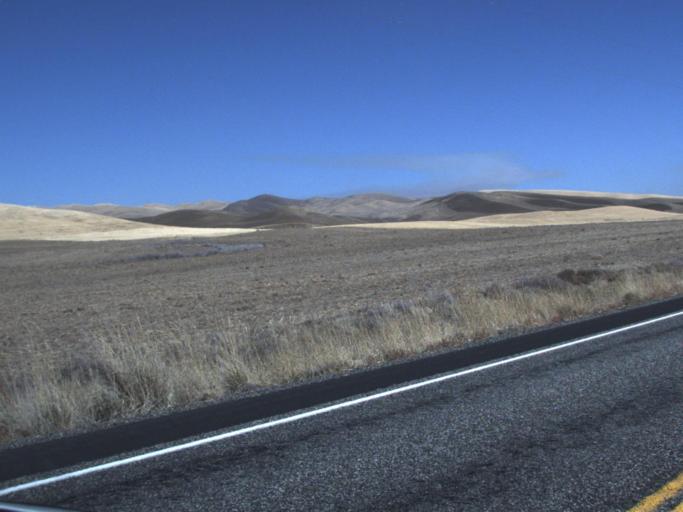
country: US
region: Washington
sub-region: Walla Walla County
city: Waitsburg
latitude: 46.3000
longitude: -118.3699
